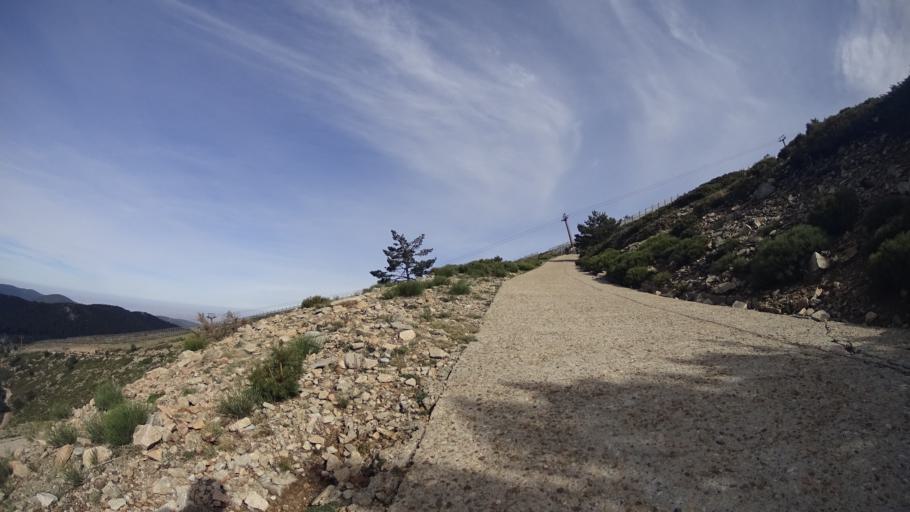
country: ES
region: Madrid
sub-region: Provincia de Madrid
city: Navacerrada
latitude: 40.7855
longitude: -3.9966
